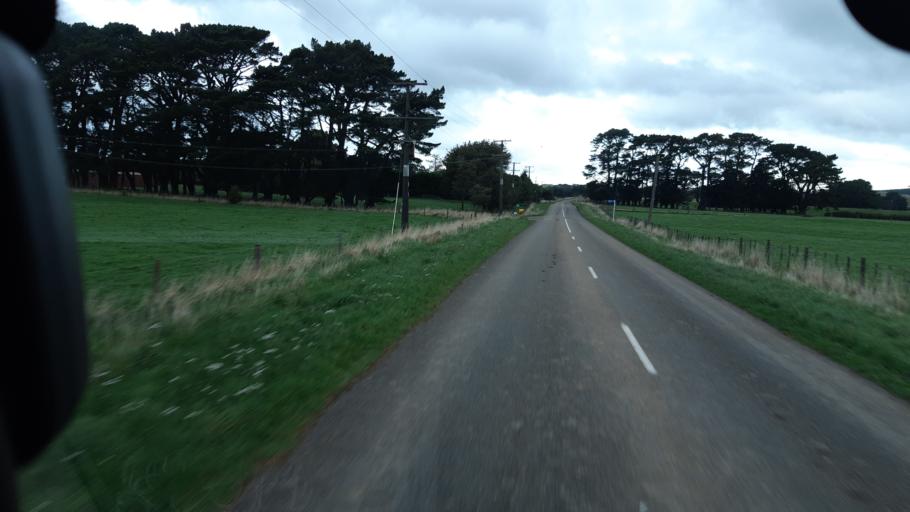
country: NZ
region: Manawatu-Wanganui
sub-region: Palmerston North City
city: Palmerston North
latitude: -40.6121
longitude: 175.6457
